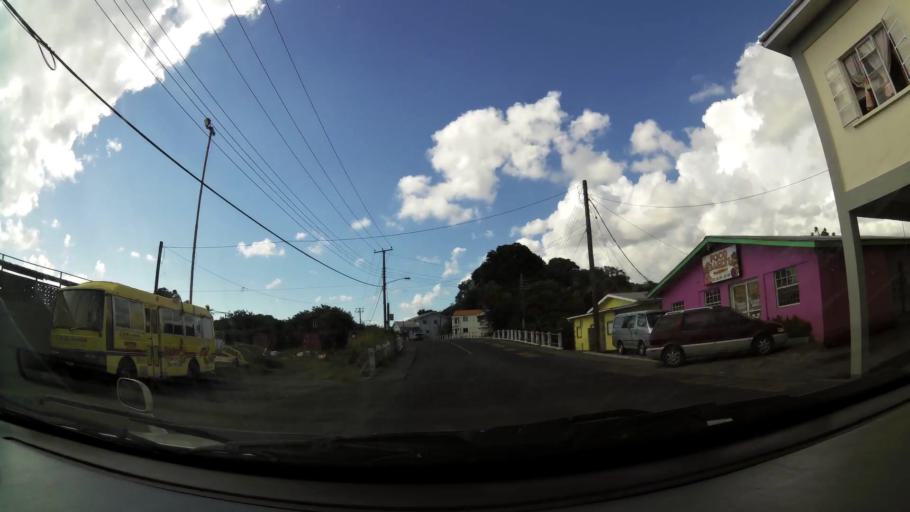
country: VC
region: Saint George
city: Kingstown
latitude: 13.1316
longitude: -61.1948
